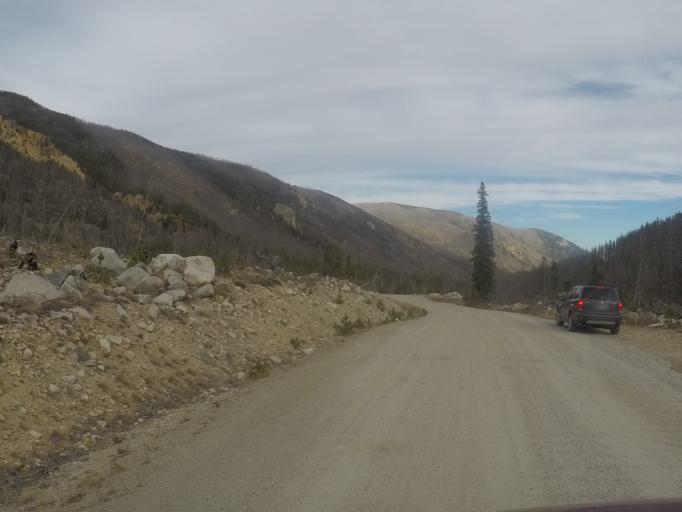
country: US
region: Montana
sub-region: Carbon County
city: Red Lodge
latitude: 45.1735
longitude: -109.4477
